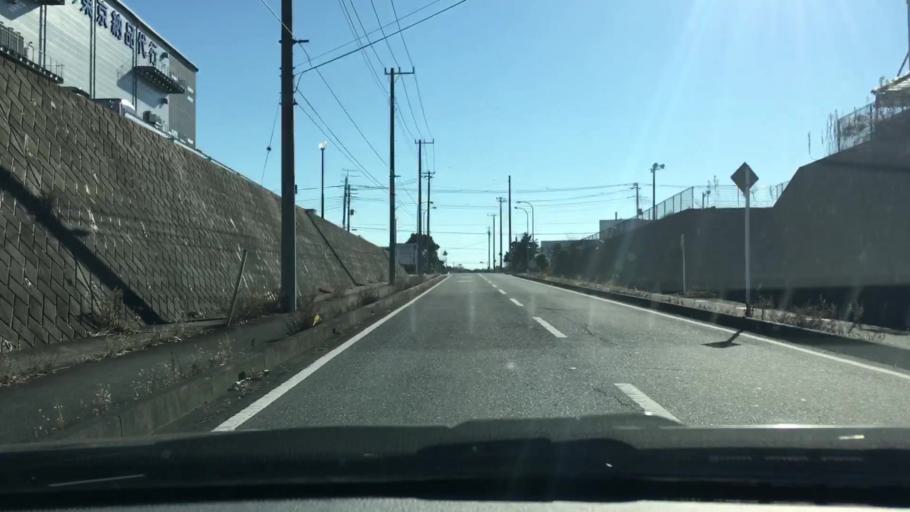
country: JP
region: Chiba
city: Shisui
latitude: 35.7155
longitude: 140.3235
